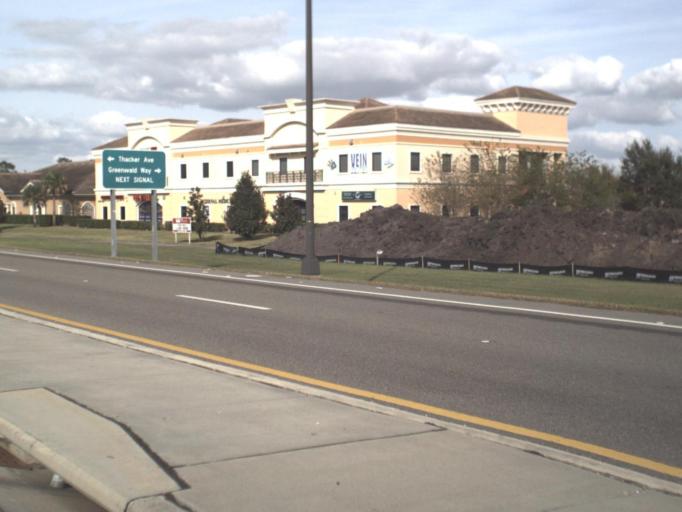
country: US
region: Florida
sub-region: Orange County
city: Hunters Creek
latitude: 28.3451
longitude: -81.4195
